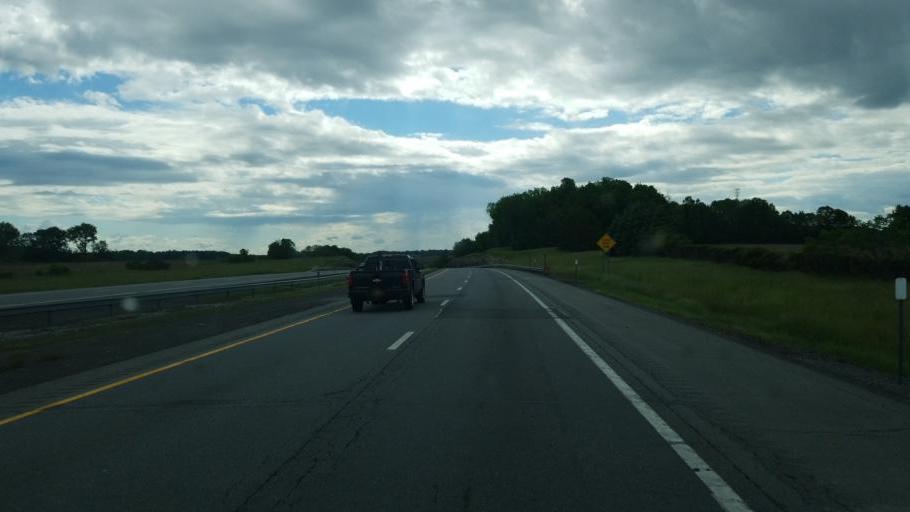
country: US
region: New York
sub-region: Ontario County
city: Phelps
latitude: 42.9693
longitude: -77.0735
